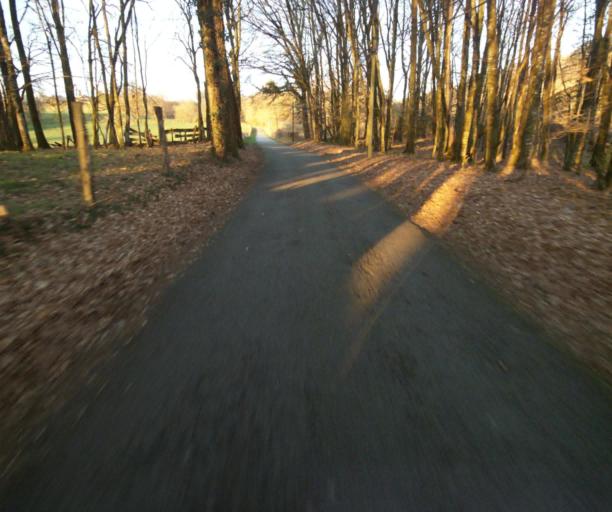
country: FR
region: Limousin
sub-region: Departement de la Correze
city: Saint-Mexant
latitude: 45.3061
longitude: 1.6318
